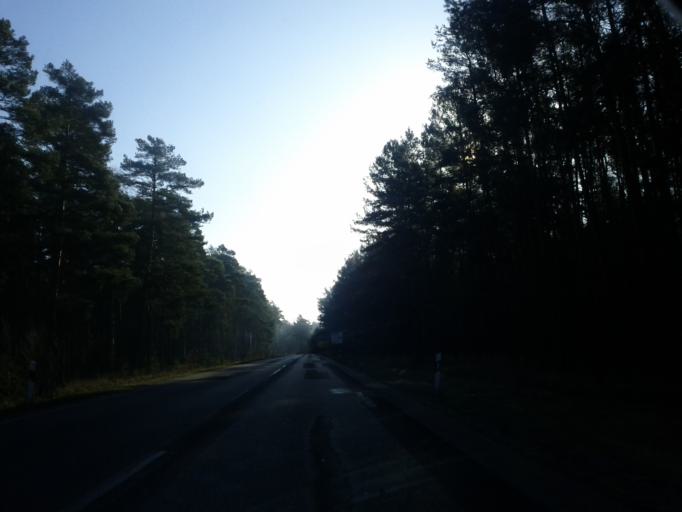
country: DE
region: Brandenburg
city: Grunheide
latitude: 52.3927
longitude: 13.8182
